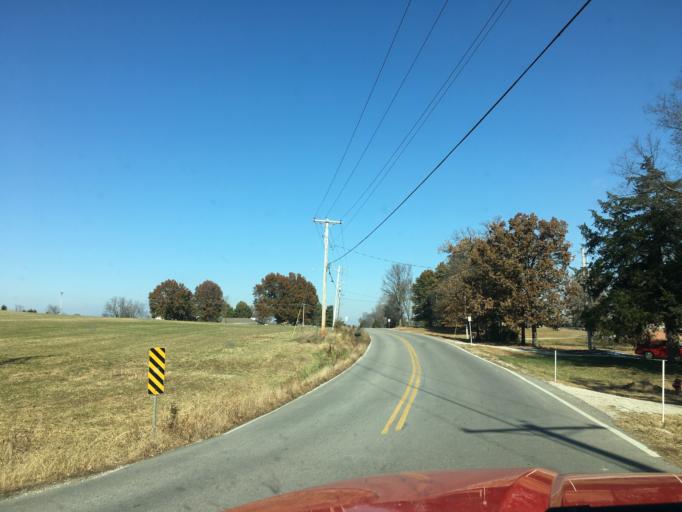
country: US
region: Missouri
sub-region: Cole County
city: Wardsville
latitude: 38.4993
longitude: -92.1764
